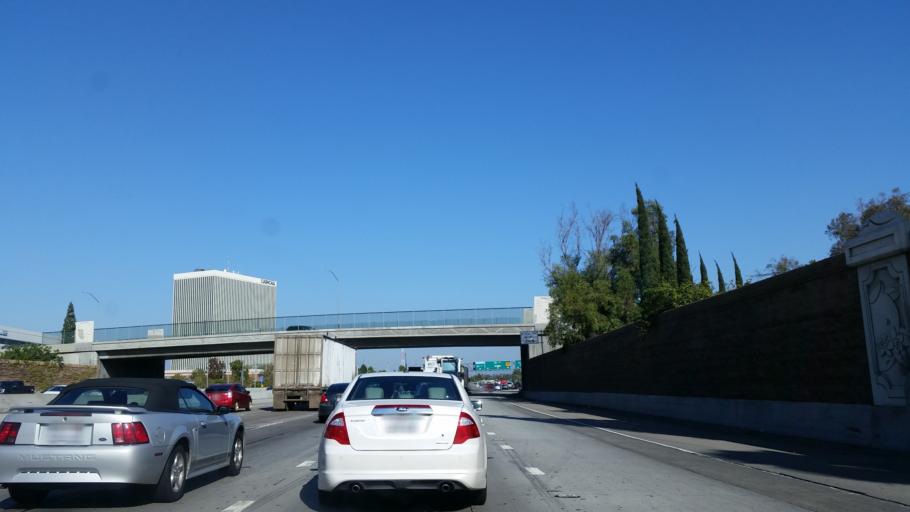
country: US
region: California
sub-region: Orange County
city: Santa Ana
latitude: 33.7779
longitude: -117.8976
